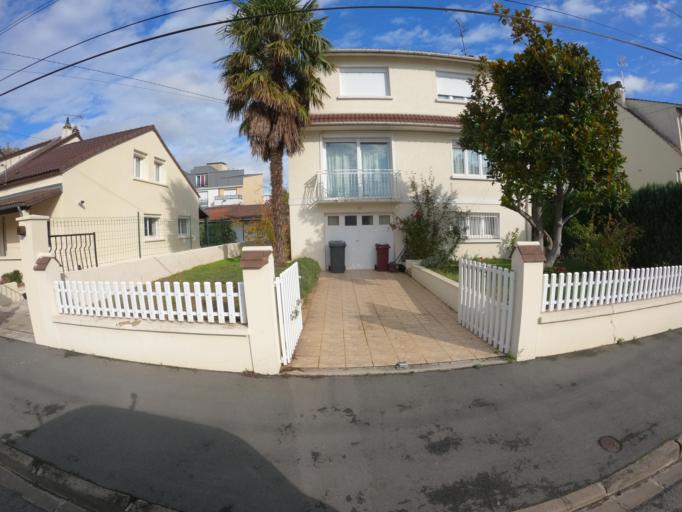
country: FR
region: Ile-de-France
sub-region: Departement de Seine-et-Marne
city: Chelles
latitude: 48.8913
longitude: 2.6124
